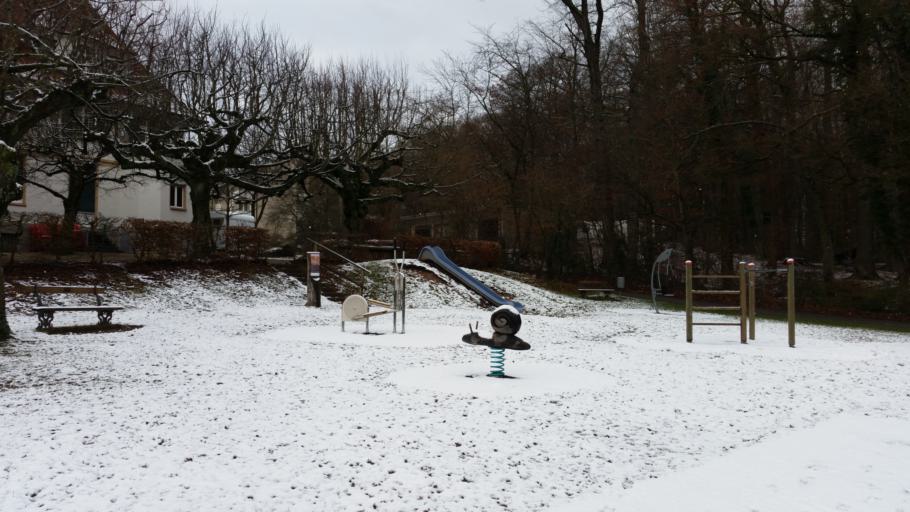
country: DE
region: Baden-Wuerttemberg
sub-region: Freiburg Region
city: Inzlingen
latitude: 47.5715
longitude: 7.6850
